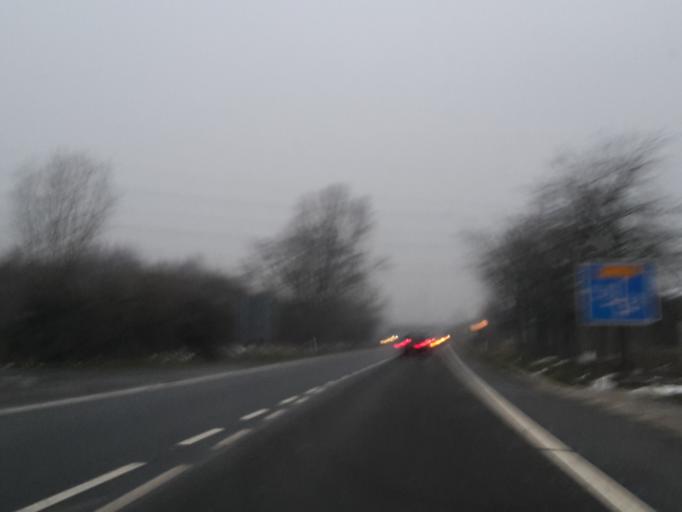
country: DE
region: Hesse
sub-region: Regierungsbezirk Darmstadt
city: Florsheim
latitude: 50.0515
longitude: 8.4336
